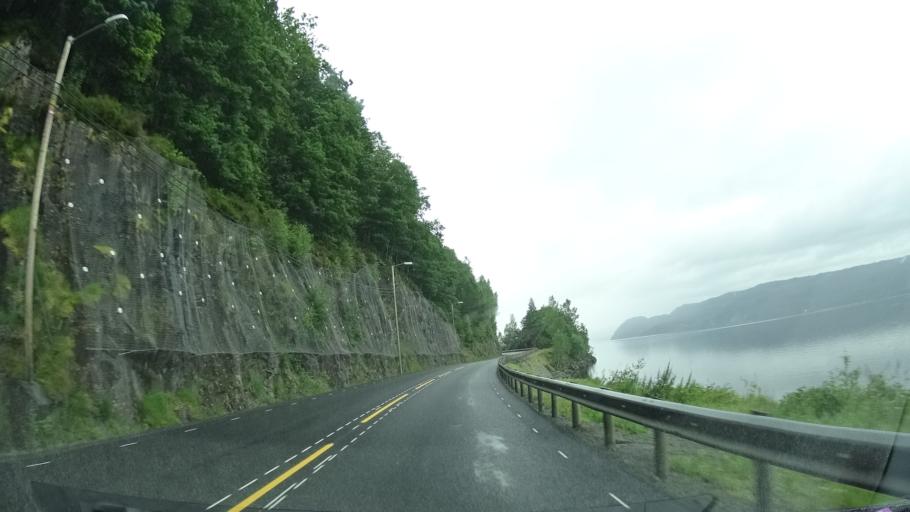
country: NO
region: Rogaland
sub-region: Lund
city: Moi
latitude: 58.4152
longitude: 6.6180
